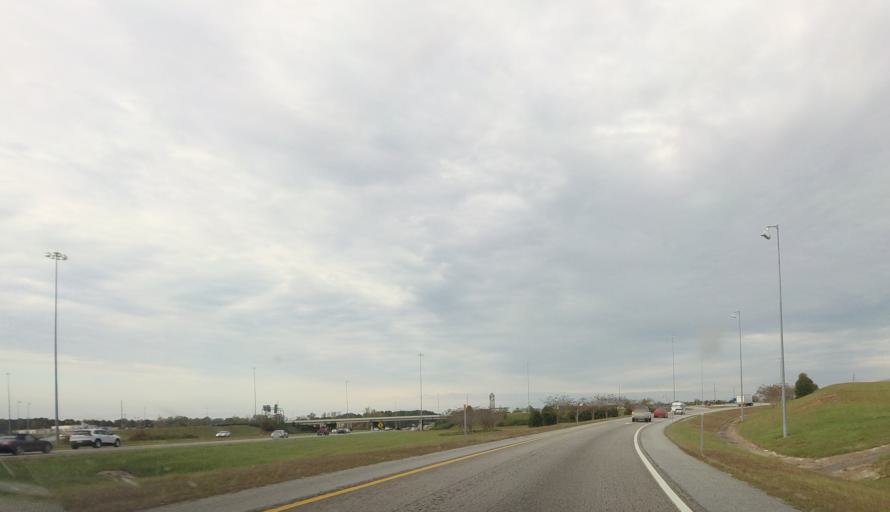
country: US
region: Alabama
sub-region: Lee County
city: Opelika
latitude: 32.6184
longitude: -85.3993
